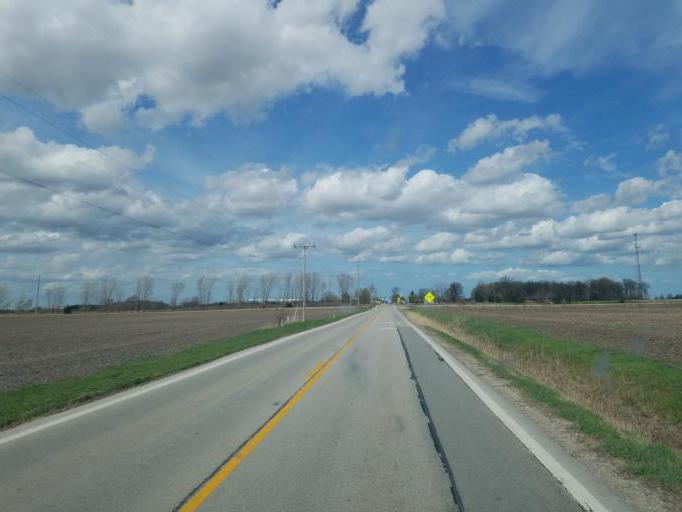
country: US
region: Ohio
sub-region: Huron County
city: Bellevue
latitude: 41.2610
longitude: -82.7967
